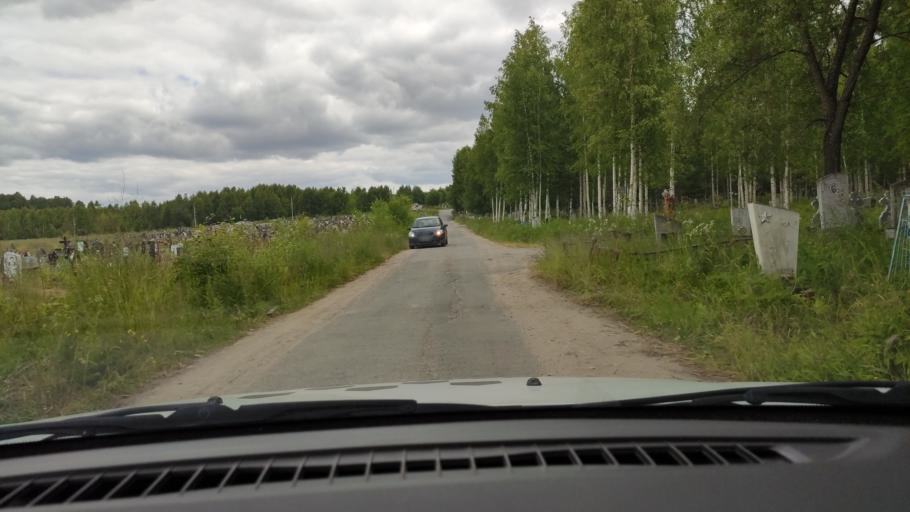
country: RU
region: Perm
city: Kondratovo
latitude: 58.0684
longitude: 56.1404
